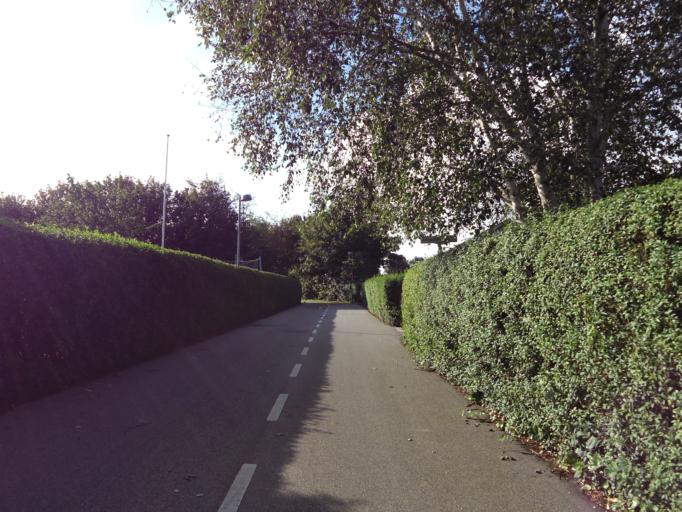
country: DK
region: South Denmark
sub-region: Esbjerg Kommune
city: Ribe
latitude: 55.3481
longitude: 8.7834
